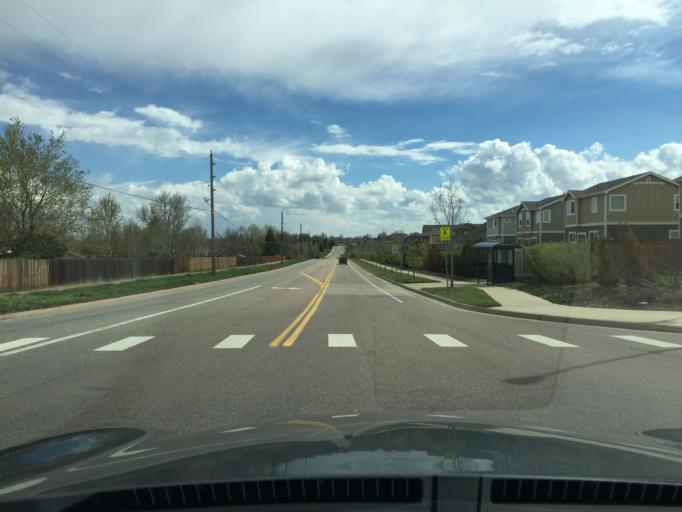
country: US
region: Colorado
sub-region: Boulder County
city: Lafayette
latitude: 40.0074
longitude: -105.0933
